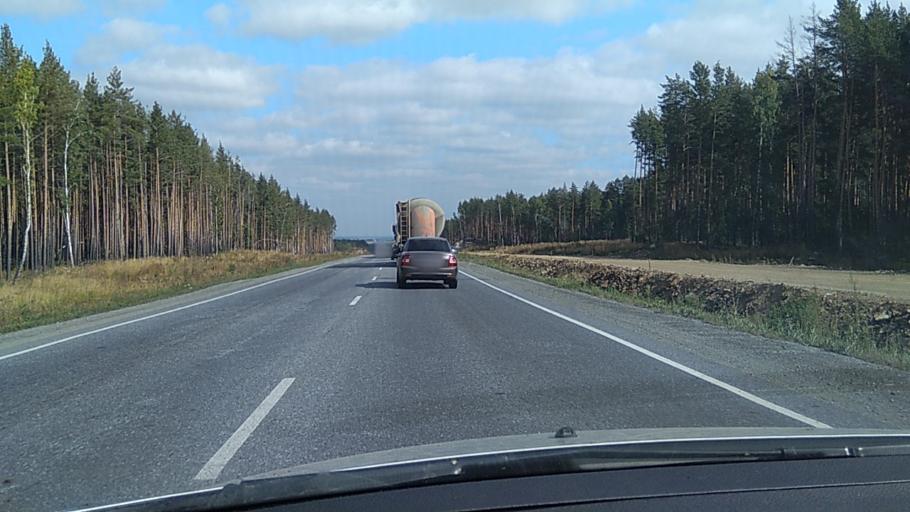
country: RU
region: Chelyabinsk
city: Chebarkul'
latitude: 54.9235
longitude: 60.2422
